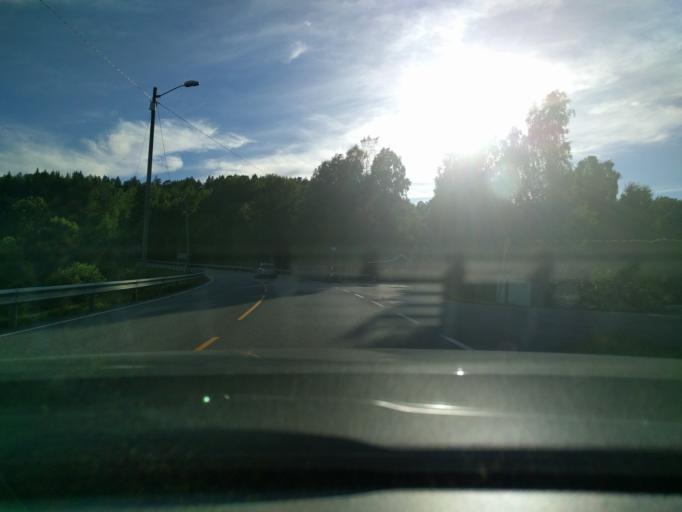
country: NO
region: Vestfold
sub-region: Hof
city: Hof
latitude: 59.4998
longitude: 10.0732
